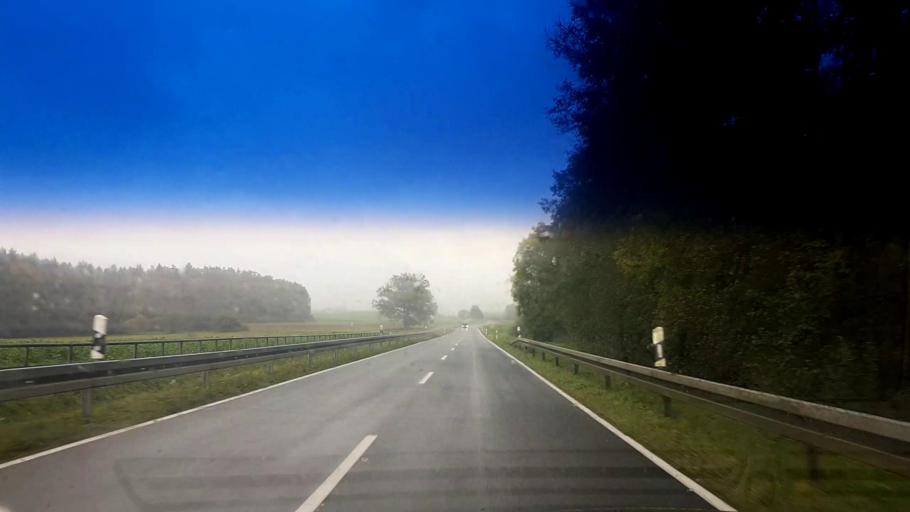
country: DE
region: Bavaria
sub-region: Upper Franconia
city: Memmelsdorf
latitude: 49.9187
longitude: 10.9753
